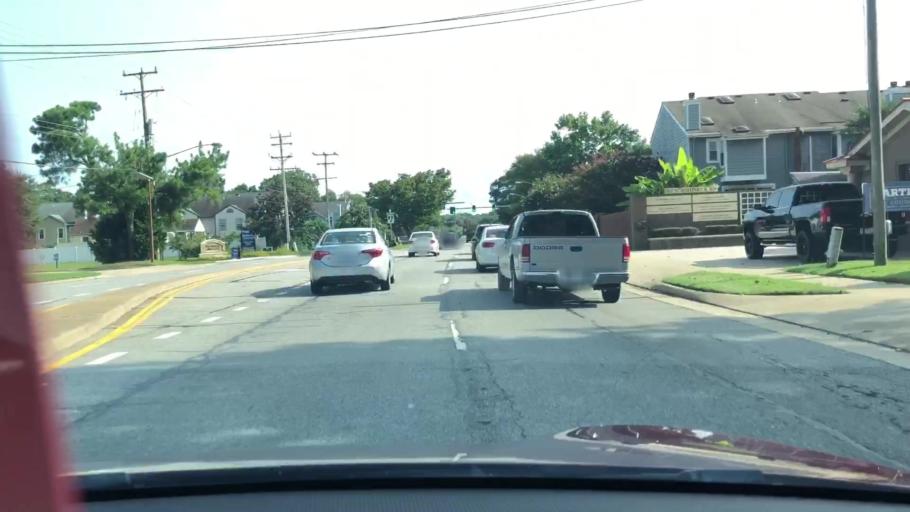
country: US
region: Virginia
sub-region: City of Virginia Beach
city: Virginia Beach
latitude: 36.8516
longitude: -75.9945
